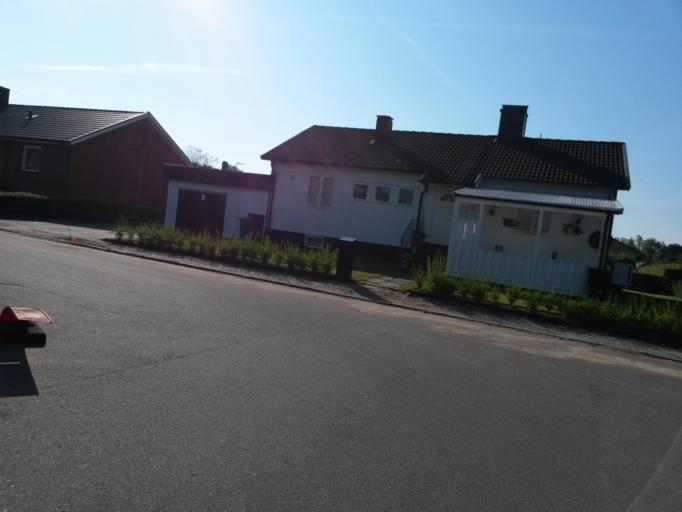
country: SE
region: Vaestra Goetaland
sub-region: Vargarda Kommun
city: Vargarda
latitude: 58.0356
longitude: 12.8147
